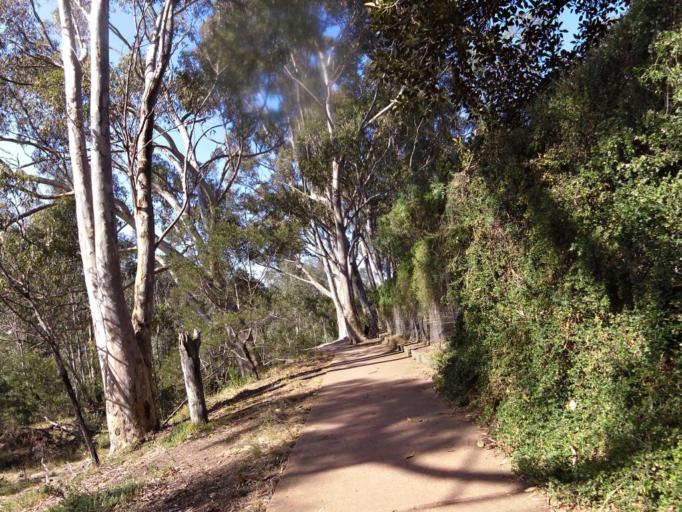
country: AU
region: Victoria
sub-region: Wyndham
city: Werribee
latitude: -37.9039
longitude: 144.6528
